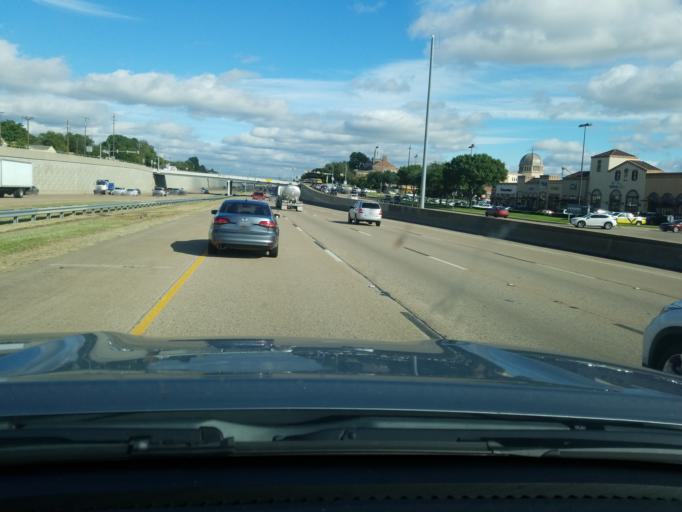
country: US
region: Texas
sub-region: Tarrant County
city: Westworth
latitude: 32.7327
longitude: -97.3903
